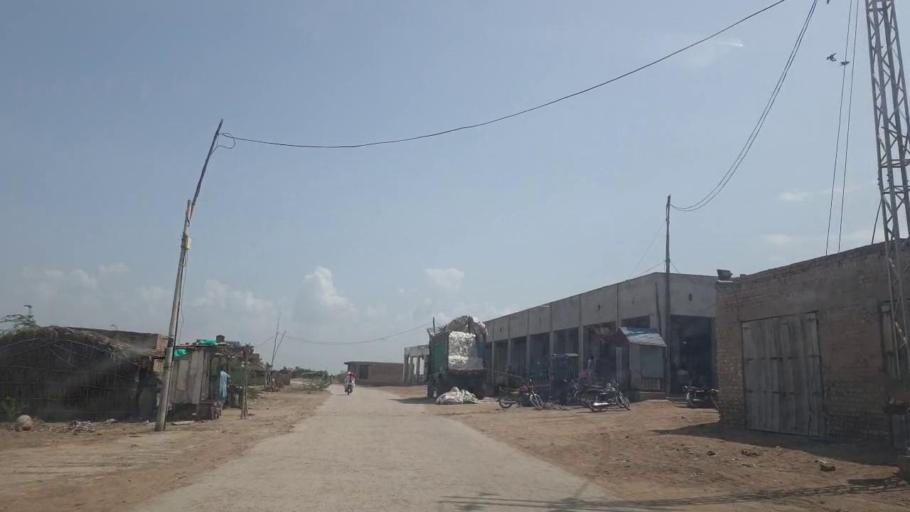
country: PK
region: Sindh
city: Naukot
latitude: 24.7582
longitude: 69.1970
